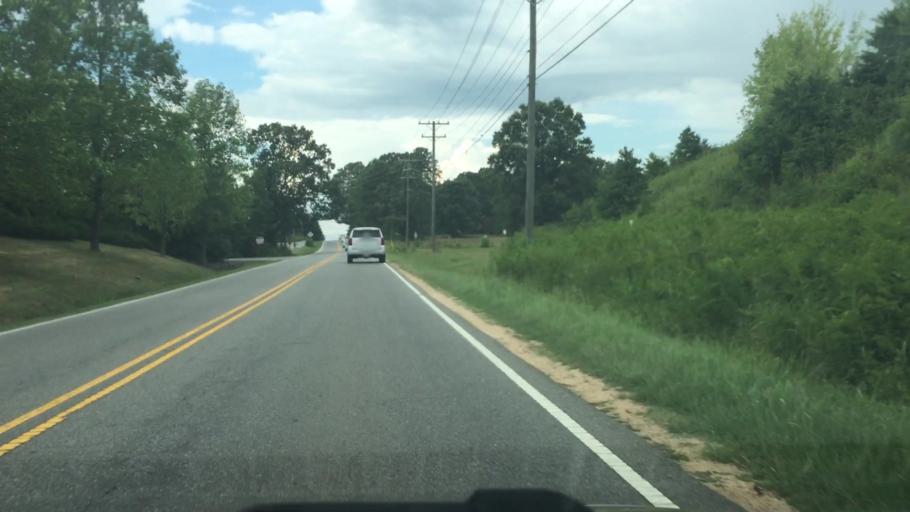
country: US
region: North Carolina
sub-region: Cabarrus County
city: Harrisburg
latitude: 35.4134
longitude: -80.7096
